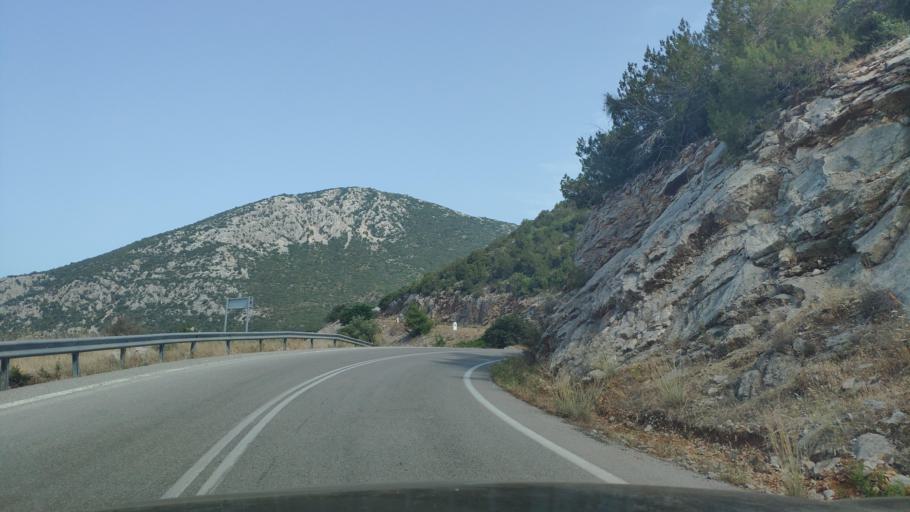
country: GR
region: Peloponnese
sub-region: Nomos Argolidos
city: Palaia Epidavros
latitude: 37.6067
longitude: 23.1558
